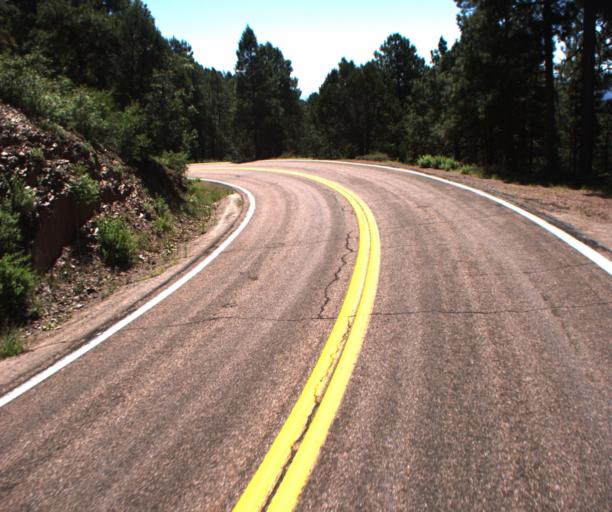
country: US
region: Arizona
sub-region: Greenlee County
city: Morenci
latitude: 33.5574
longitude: -109.3268
